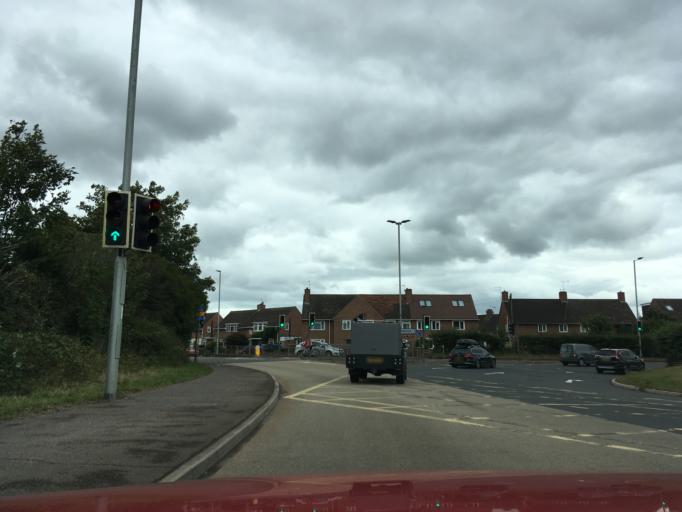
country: GB
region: England
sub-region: Devon
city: Heavitree
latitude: 50.7006
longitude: -3.4930
